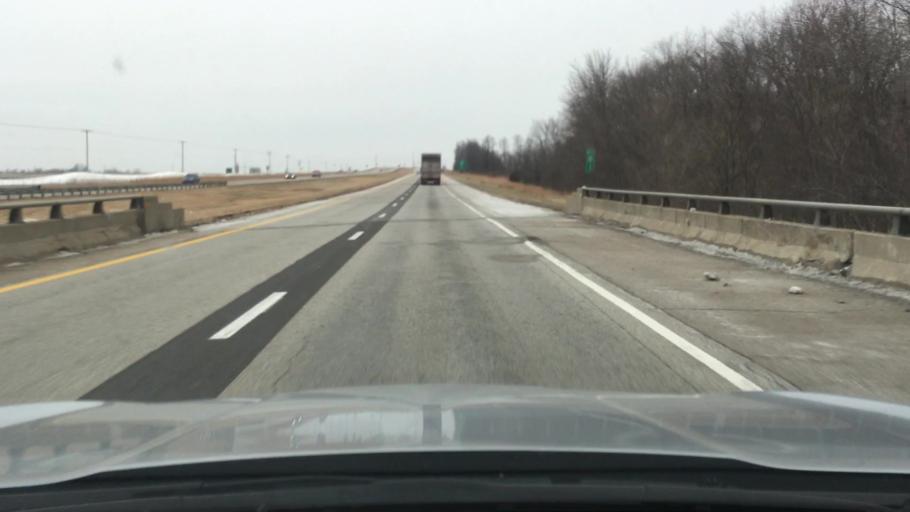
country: US
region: Illinois
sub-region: Sangamon County
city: Divernon
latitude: 39.5804
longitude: -89.6462
